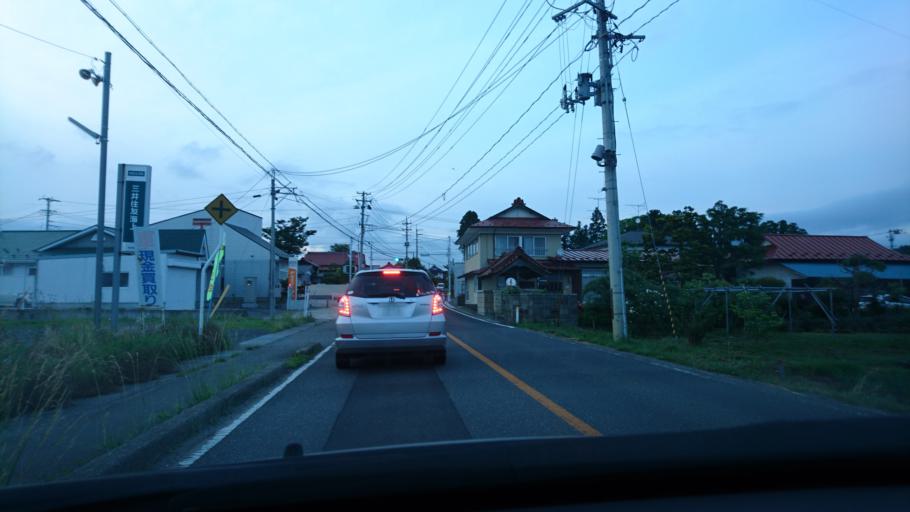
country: JP
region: Iwate
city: Ichinoseki
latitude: 38.8087
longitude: 140.9836
